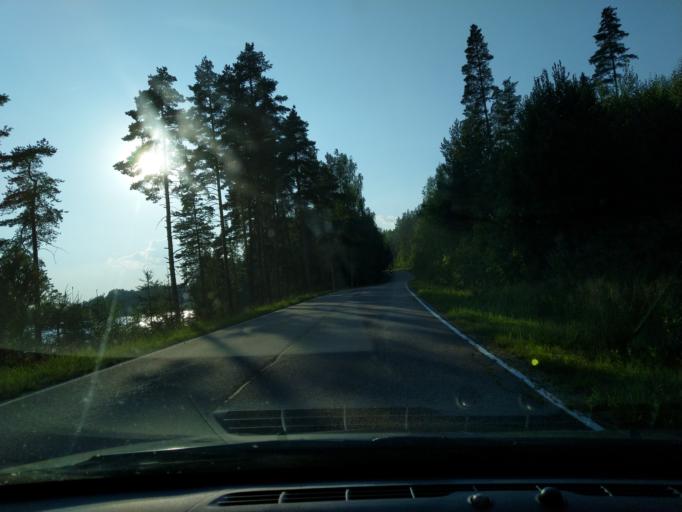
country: FI
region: Uusimaa
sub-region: Helsinki
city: Vihti
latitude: 60.5316
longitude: 24.3508
